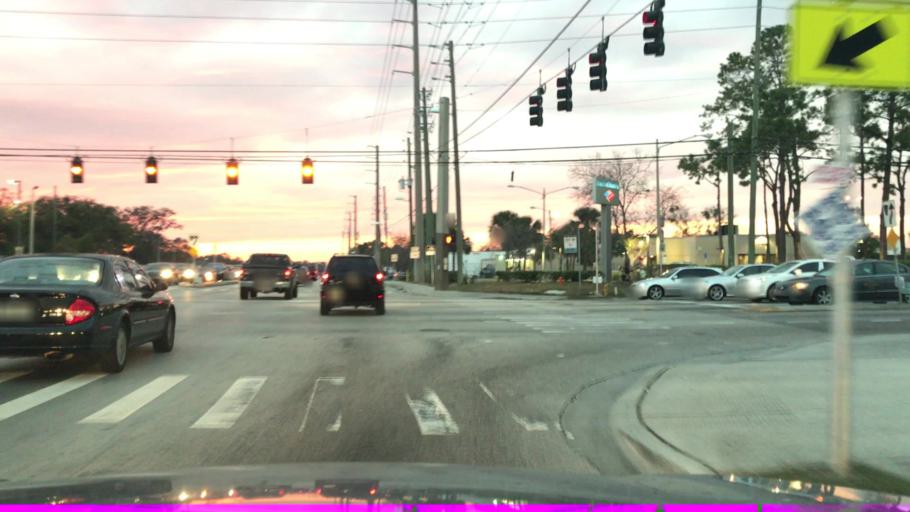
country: US
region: Florida
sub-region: Orange County
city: Pine Hills
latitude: 28.5777
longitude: -81.4758
